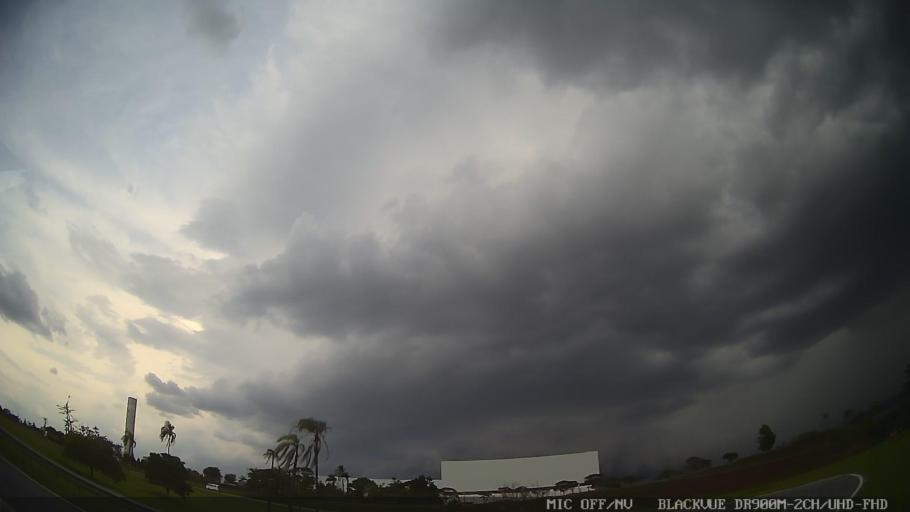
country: BR
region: Sao Paulo
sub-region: Itatiba
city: Itatiba
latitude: -22.9757
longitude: -46.8354
